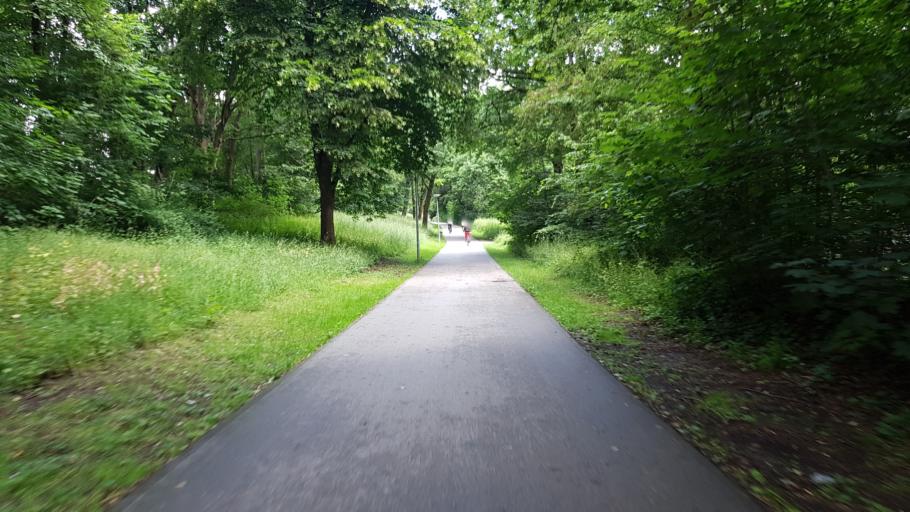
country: DE
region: Bavaria
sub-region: Upper Bavaria
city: Pasing
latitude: 48.1241
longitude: 11.4748
